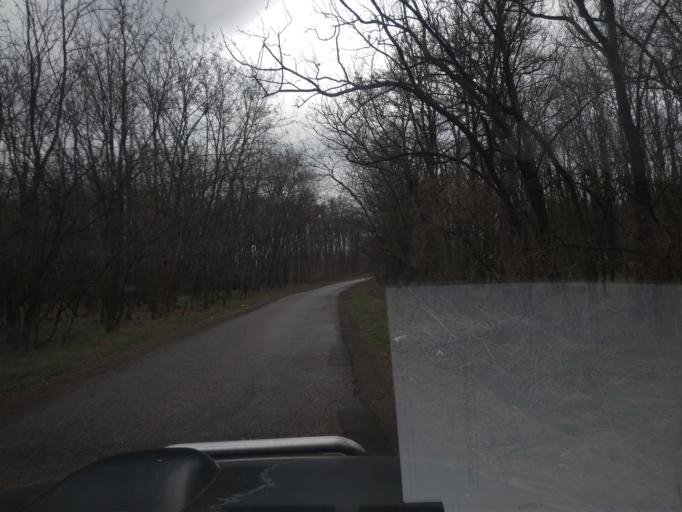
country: HU
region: Szabolcs-Szatmar-Bereg
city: Nyirpazony
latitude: 48.0222
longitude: 21.8045
